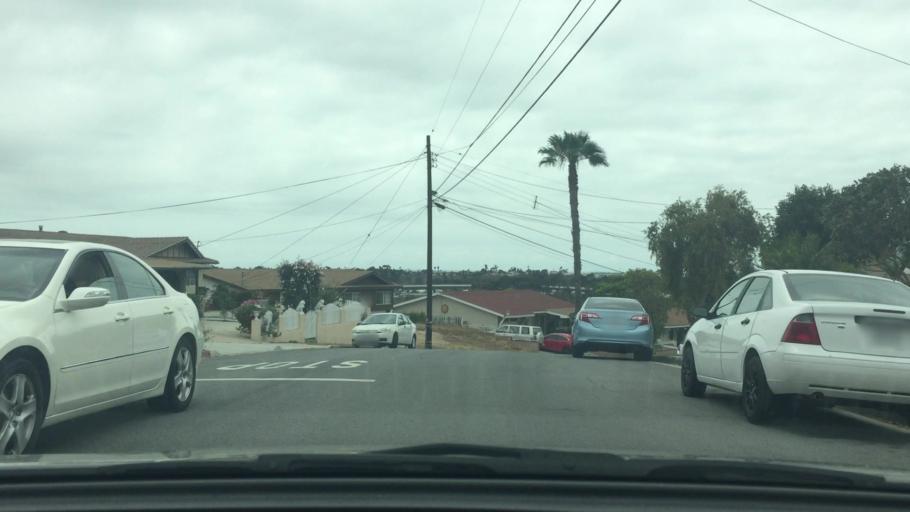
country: US
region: California
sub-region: San Diego County
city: Chula Vista
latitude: 32.6604
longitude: -117.0636
